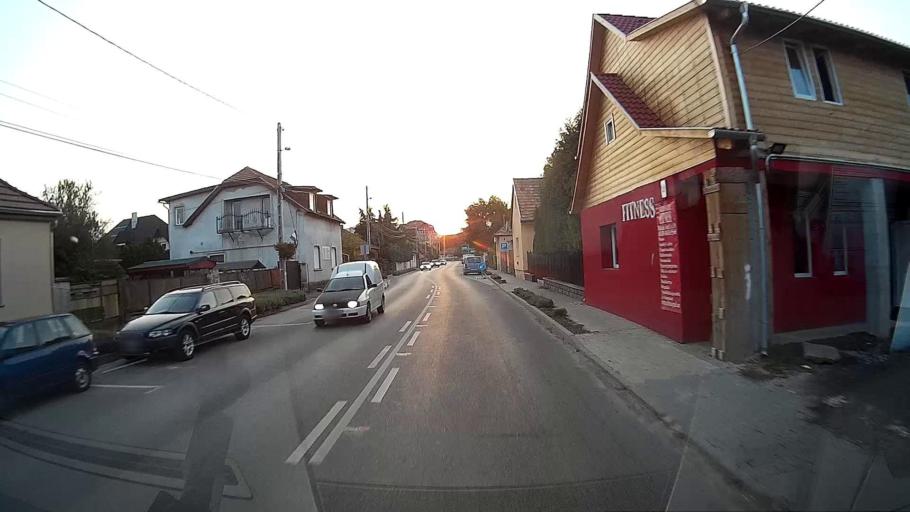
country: HU
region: Pest
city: Budakalasz
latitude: 47.6219
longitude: 19.0527
